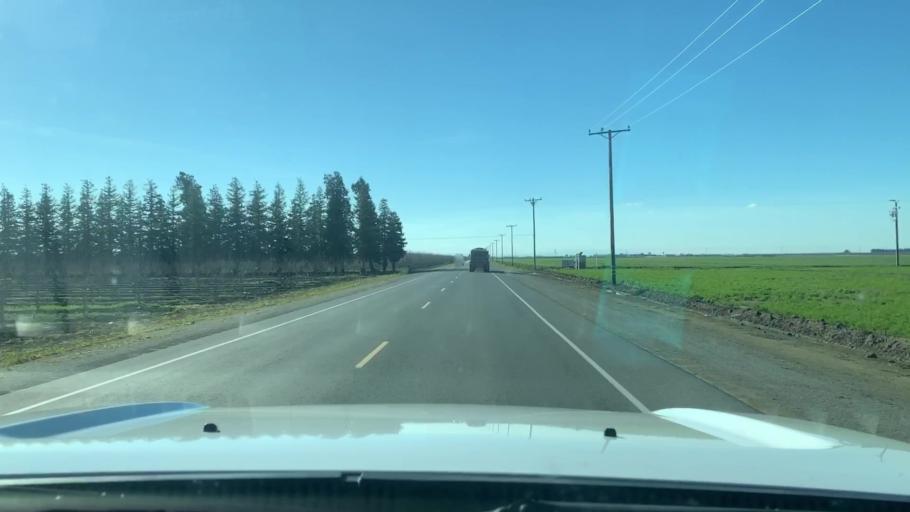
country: US
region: California
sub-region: Kings County
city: Corcoran
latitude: 36.2109
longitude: -119.5005
